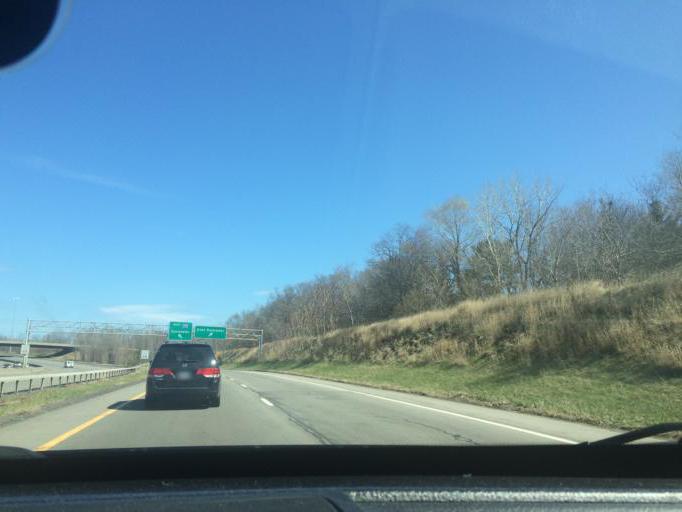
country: US
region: New York
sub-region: Monroe County
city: East Rochester
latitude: 43.1137
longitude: -77.5061
